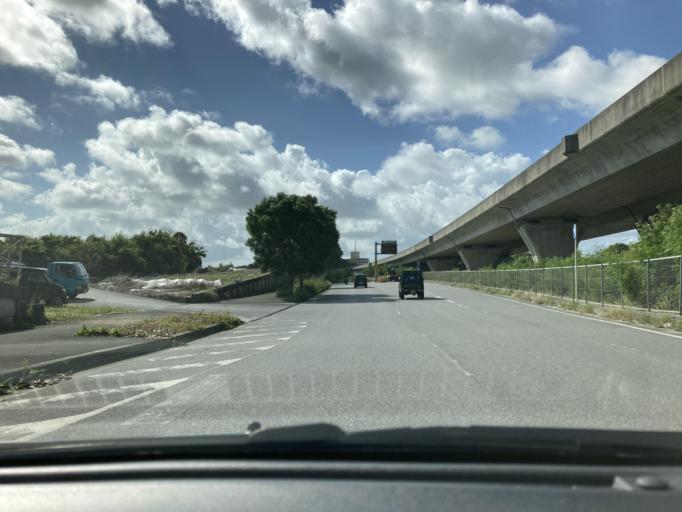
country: JP
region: Okinawa
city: Tomigusuku
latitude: 26.1809
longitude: 127.7236
